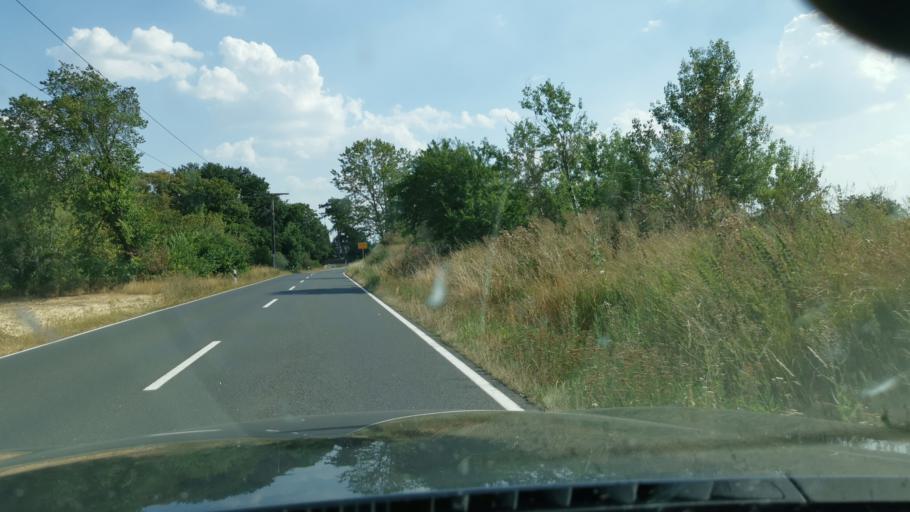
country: DE
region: Saxony
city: Zschepplin
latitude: 51.5076
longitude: 12.6023
